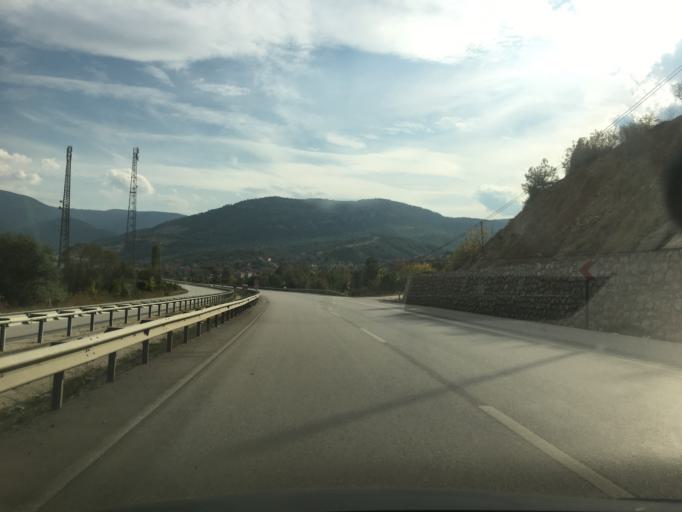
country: TR
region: Karabuk
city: Karabuk
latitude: 41.1110
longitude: 32.6692
